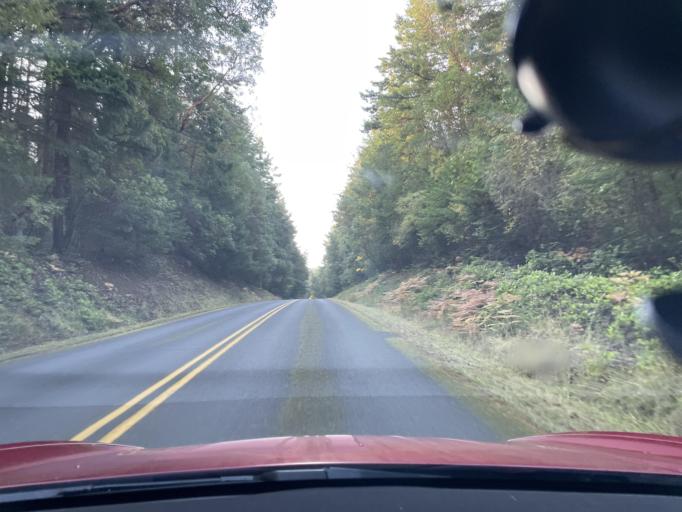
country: US
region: Washington
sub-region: San Juan County
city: Friday Harbor
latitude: 48.5459
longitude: -123.1590
